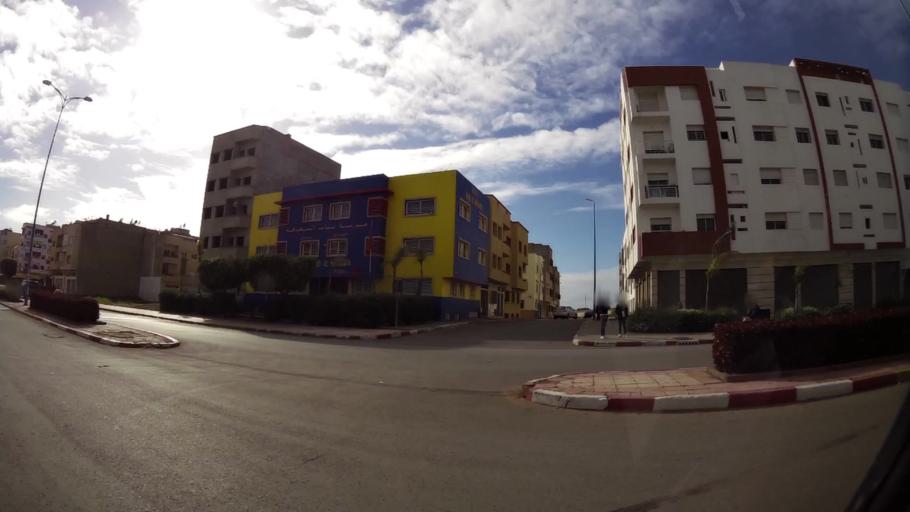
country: MA
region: Grand Casablanca
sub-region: Mohammedia
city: Mohammedia
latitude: 33.7019
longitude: -7.3607
